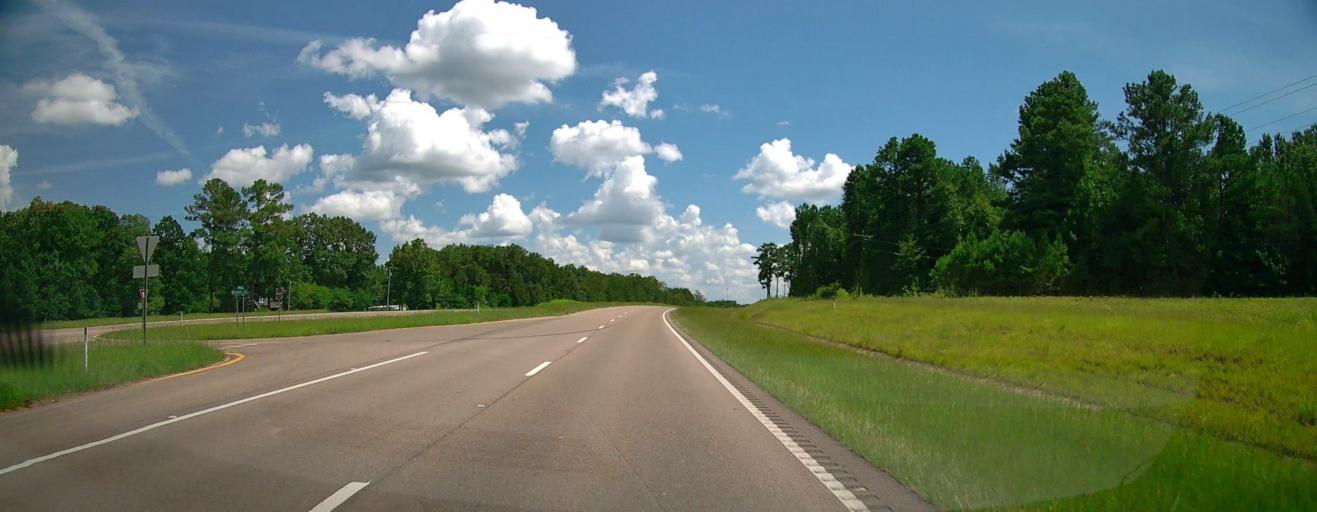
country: US
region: Mississippi
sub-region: Monroe County
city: Amory
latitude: 33.9408
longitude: -88.5986
